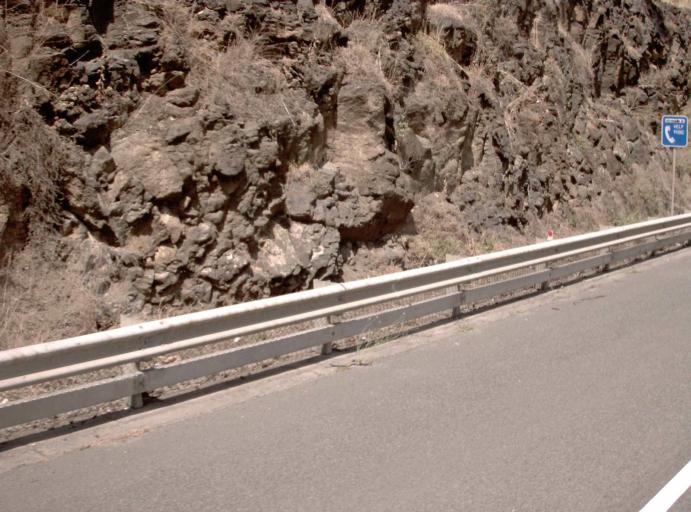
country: AU
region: Victoria
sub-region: Darebin
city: Fairfield
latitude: -37.7919
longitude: 145.0126
